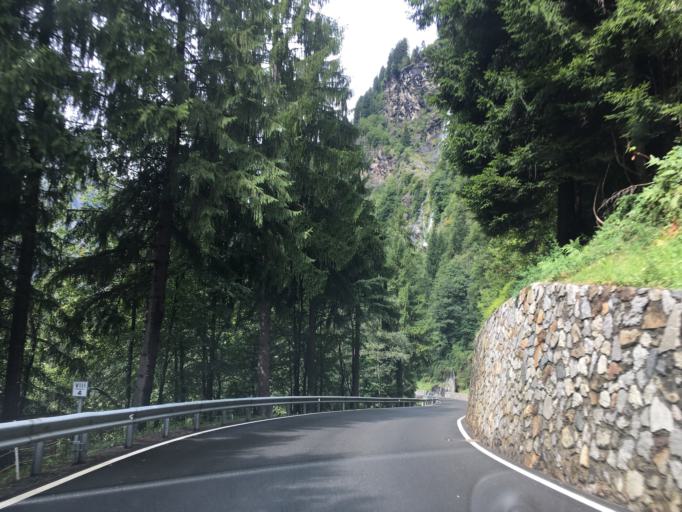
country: IT
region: Trentino-Alto Adige
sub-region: Bolzano
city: Moso in Passiria
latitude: 46.8232
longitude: 11.1948
